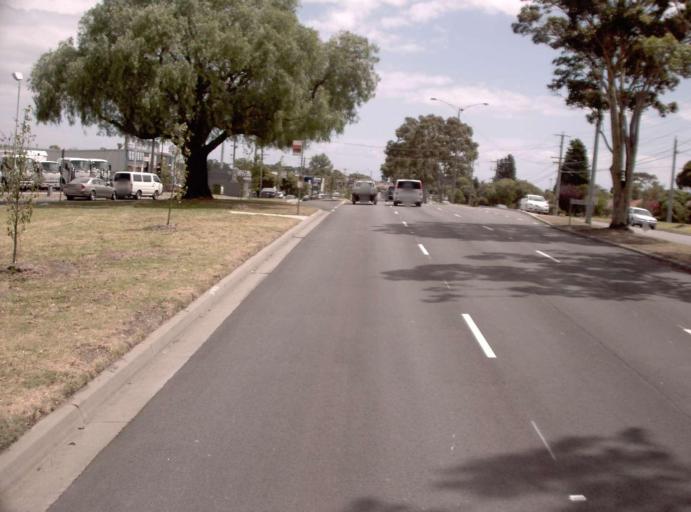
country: AU
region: Victoria
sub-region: Greater Dandenong
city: Keysborough
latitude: -37.9941
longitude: 145.1860
